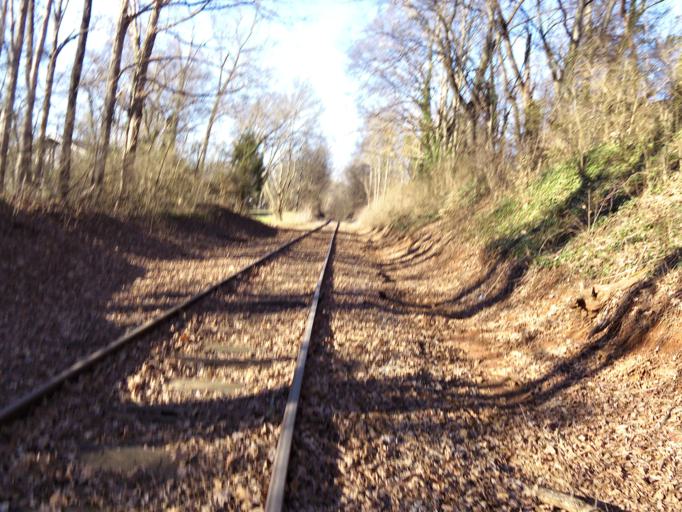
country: US
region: Tennessee
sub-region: Knox County
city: Knoxville
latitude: 35.9507
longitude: -83.8772
